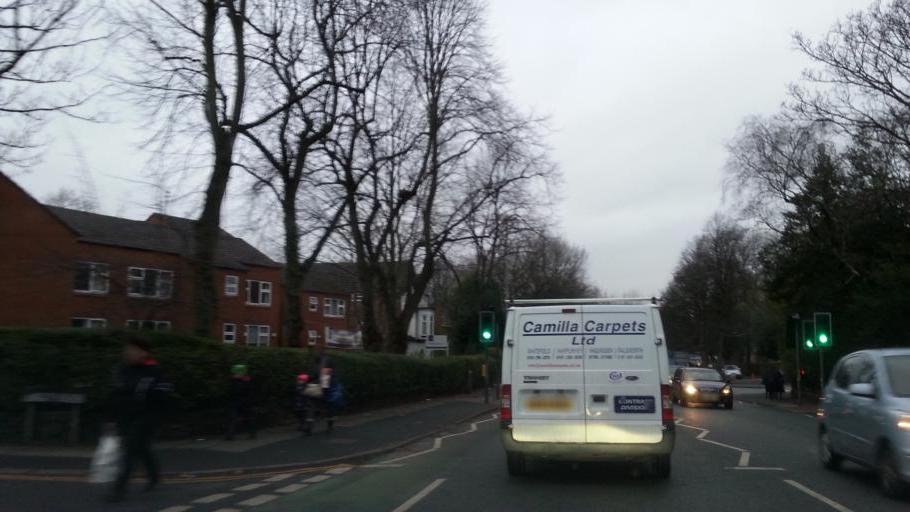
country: GB
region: England
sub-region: Borough of Bury
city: Prestwich
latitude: 53.5159
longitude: -2.2701
